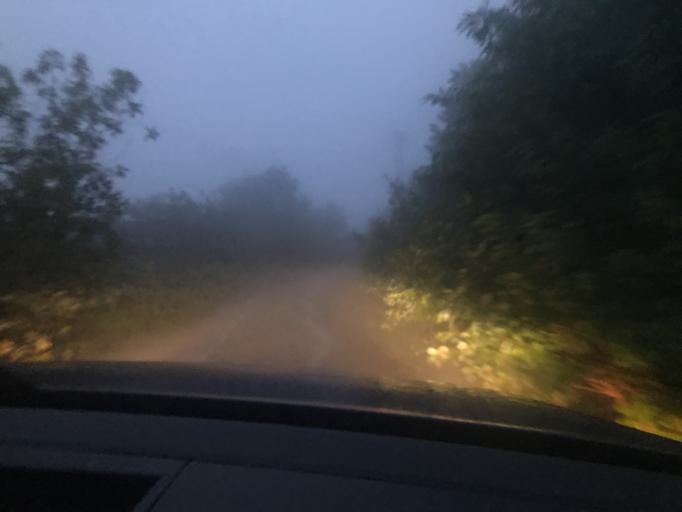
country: TR
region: Trabzon
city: Hayrat
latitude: 40.8298
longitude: 40.3877
